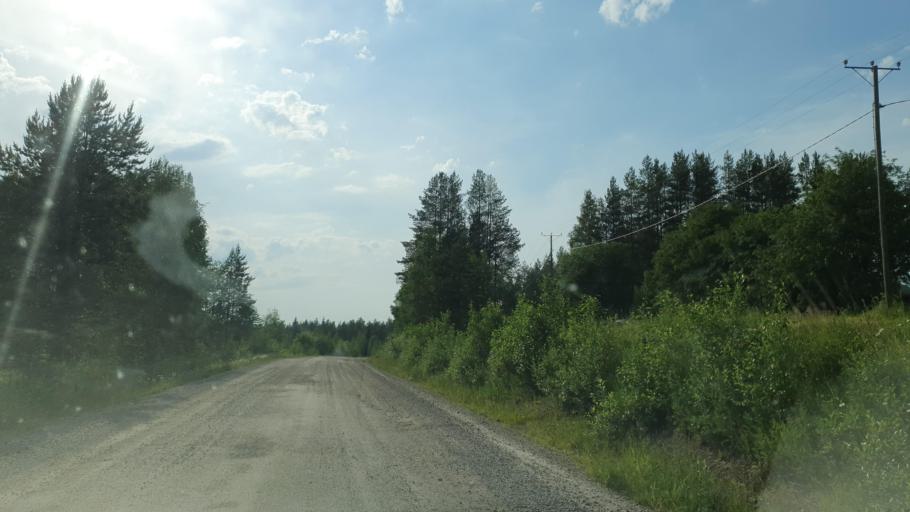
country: FI
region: Kainuu
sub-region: Kehys-Kainuu
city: Kuhmo
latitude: 64.1026
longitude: 29.5422
